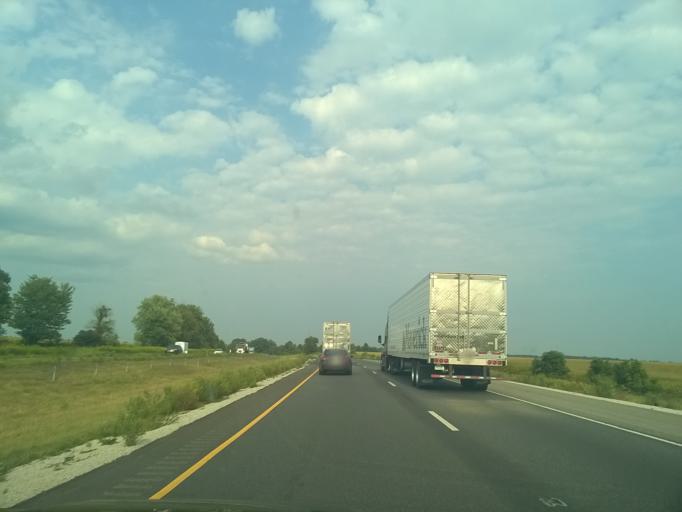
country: US
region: Indiana
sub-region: Clay County
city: Brazil
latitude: 39.4698
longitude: -87.0317
